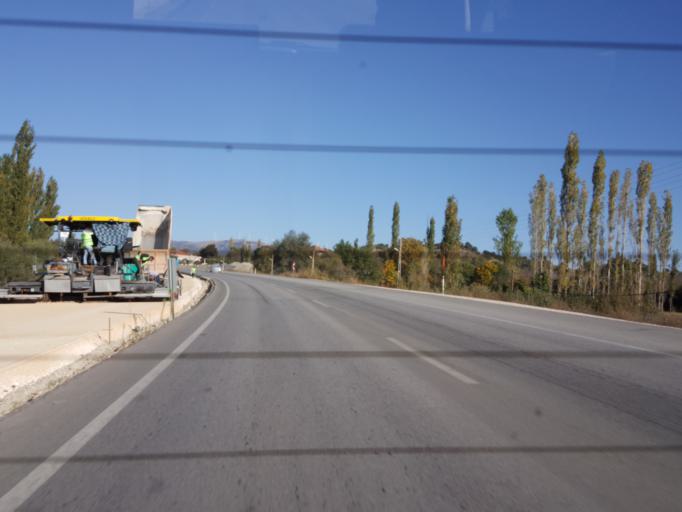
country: TR
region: Amasya
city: Ezinepazari
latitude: 40.5482
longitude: 36.1510
